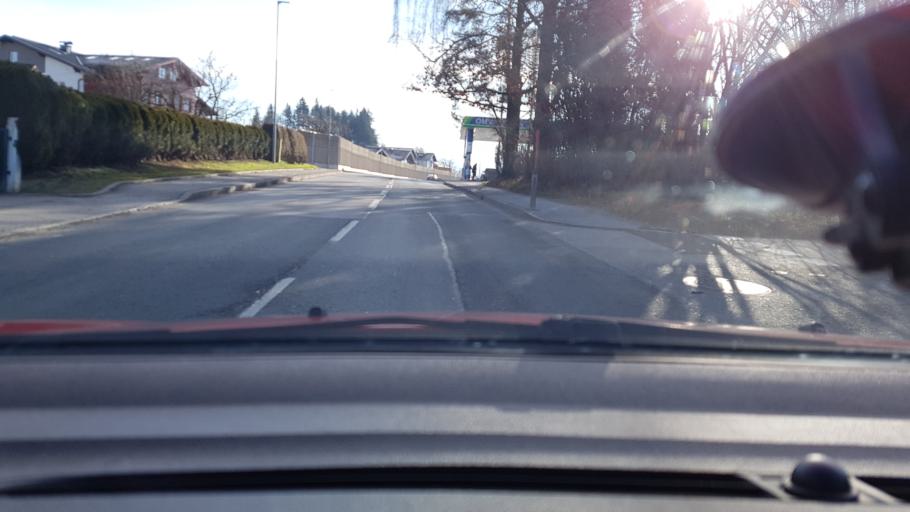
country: AT
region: Salzburg
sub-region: Politischer Bezirk Salzburg-Umgebung
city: Lamprechtshausen
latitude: 47.9872
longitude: 12.9546
